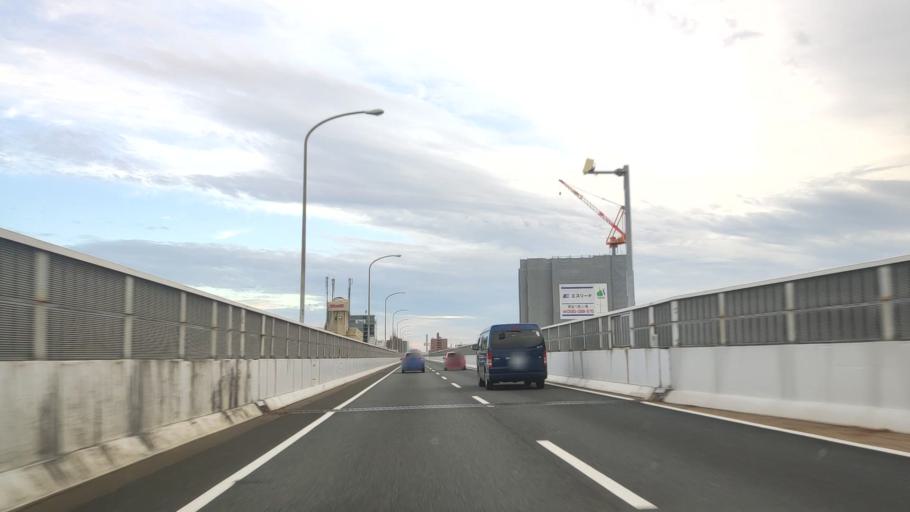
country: JP
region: Aichi
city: Nagoya-shi
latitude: 35.1917
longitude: 136.9127
